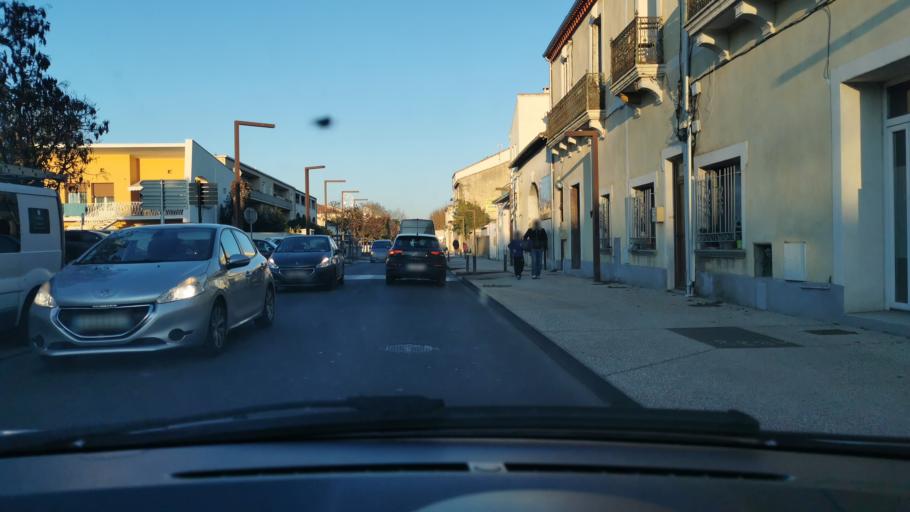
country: FR
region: Languedoc-Roussillon
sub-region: Departement de l'Herault
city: Frontignan
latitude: 43.4456
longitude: 3.7522
